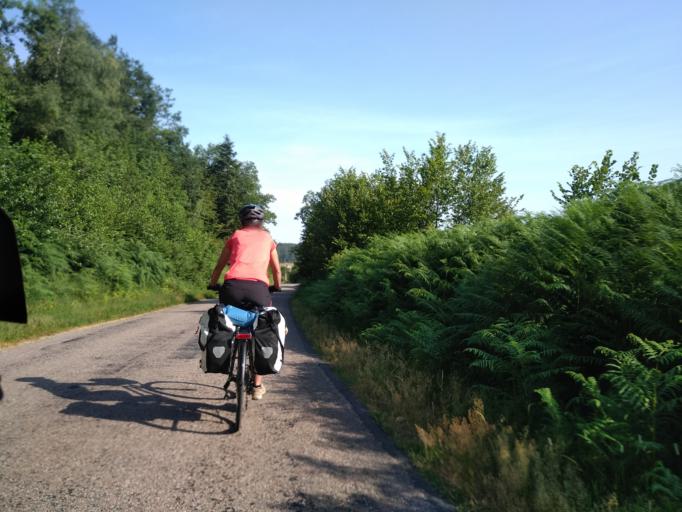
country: FR
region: Bourgogne
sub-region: Departement de Saone-et-Loire
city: Marcigny
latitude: 46.2514
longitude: 4.1143
